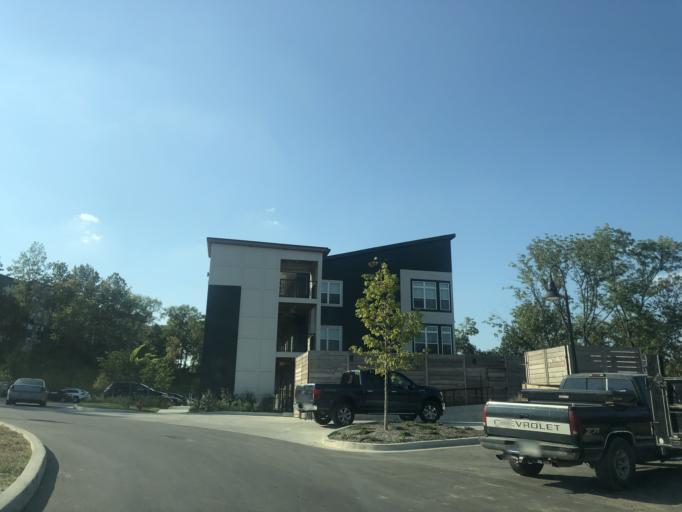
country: US
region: Tennessee
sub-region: Davidson County
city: Belle Meade
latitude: 36.1341
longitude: -86.8978
